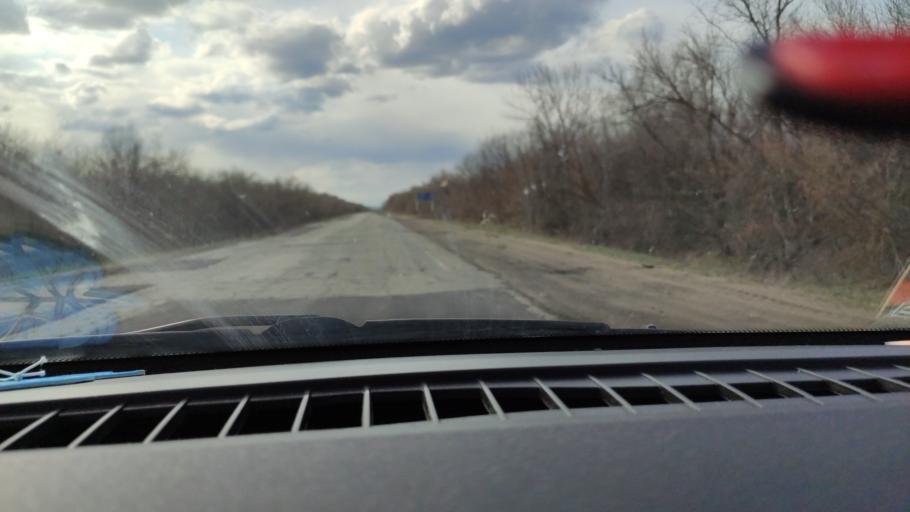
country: RU
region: Saratov
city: Krasnoarmeysk
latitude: 51.0791
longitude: 45.9692
